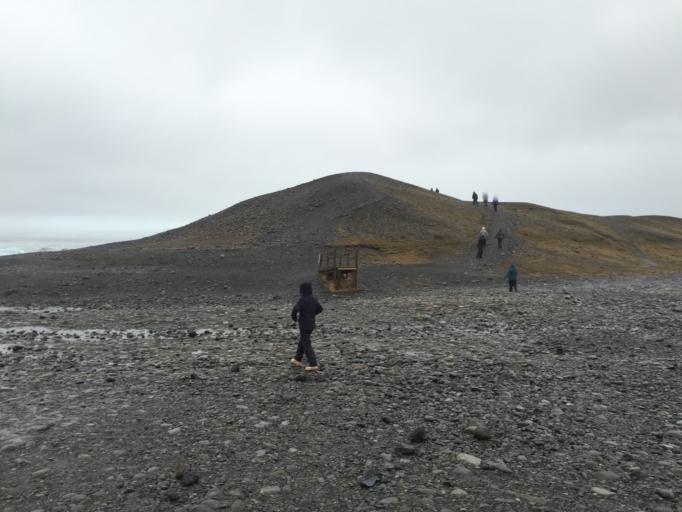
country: IS
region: East
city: Hoefn
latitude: 64.0484
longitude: -16.1796
